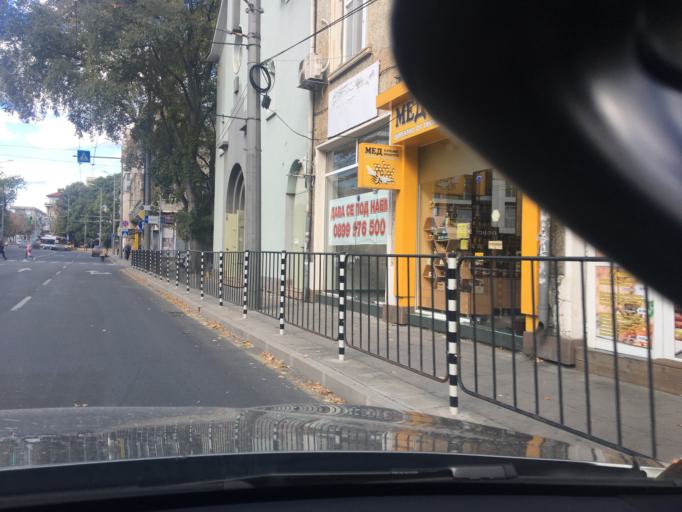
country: BG
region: Burgas
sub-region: Obshtina Burgas
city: Burgas
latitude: 42.4920
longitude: 27.4716
